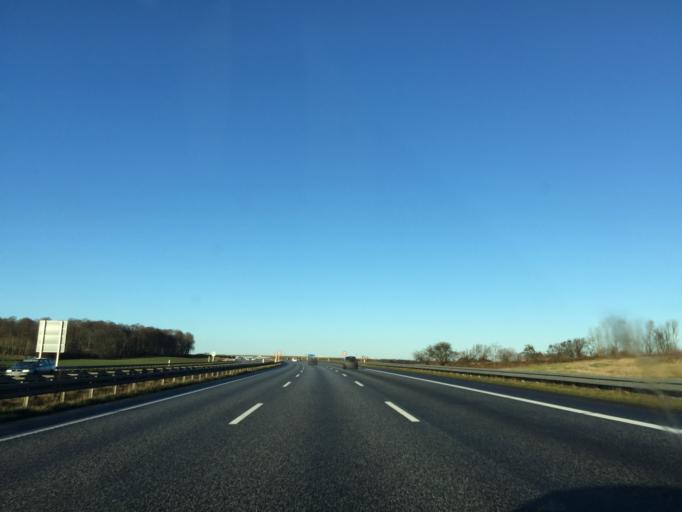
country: DK
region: South Denmark
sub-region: Vejle Kommune
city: Vejle
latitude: 55.6558
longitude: 9.5605
